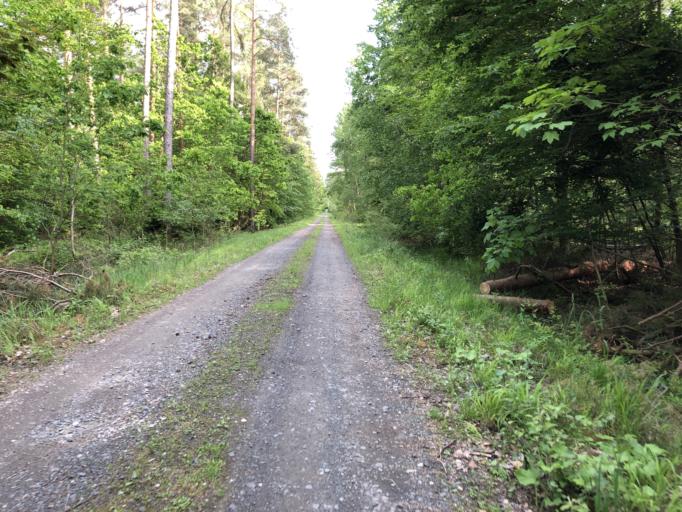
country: DE
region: Bavaria
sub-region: Upper Franconia
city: Memmelsdorf
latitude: 49.9089
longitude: 10.9571
